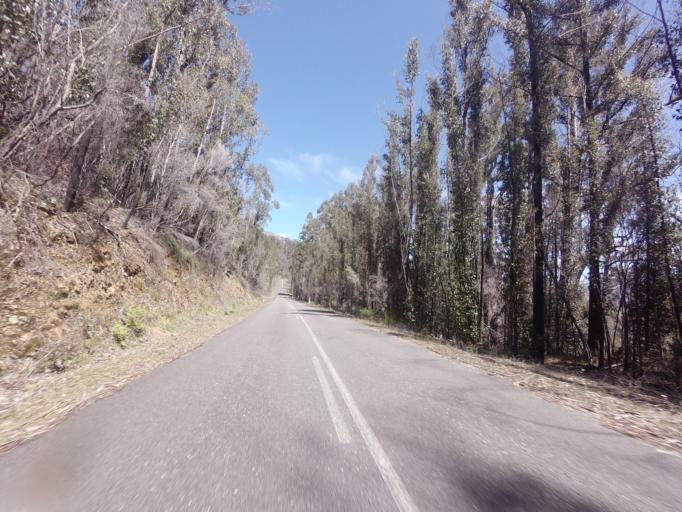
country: AU
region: Tasmania
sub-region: Huon Valley
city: Geeveston
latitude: -42.8413
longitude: 146.2538
